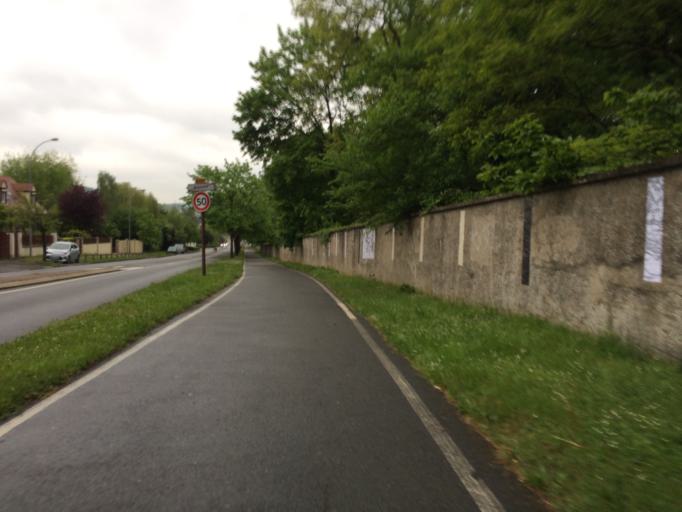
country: FR
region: Ile-de-France
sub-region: Departement de l'Essonne
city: Palaiseau
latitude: 48.7324
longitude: 2.2418
